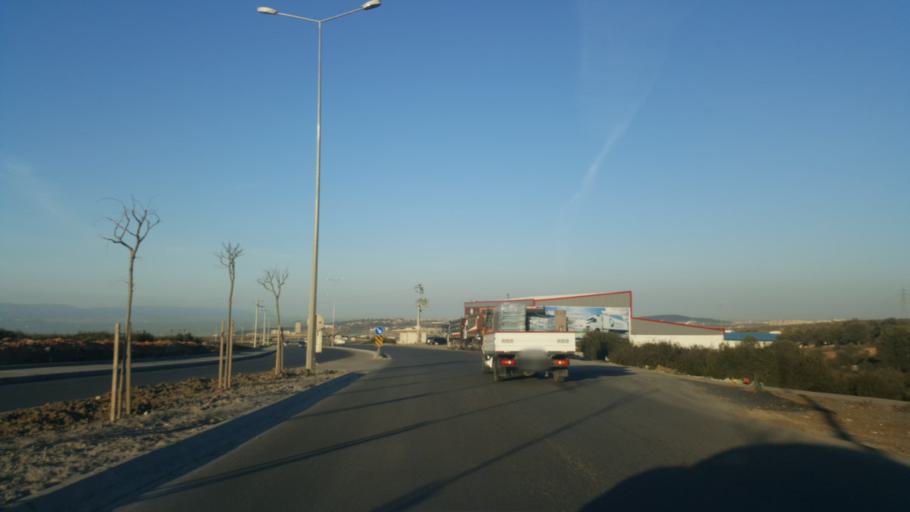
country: TR
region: Kocaeli
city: Tavsancil
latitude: 40.8065
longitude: 29.5568
